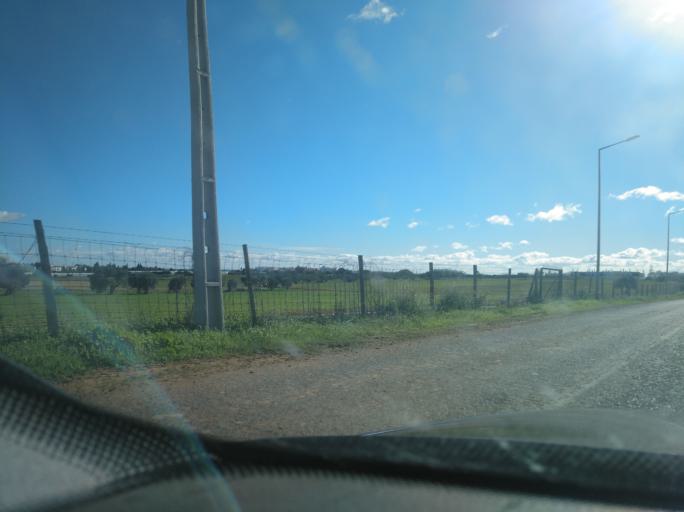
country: PT
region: Faro
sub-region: Vila Real de Santo Antonio
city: Monte Gordo
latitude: 37.1752
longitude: -7.5201
